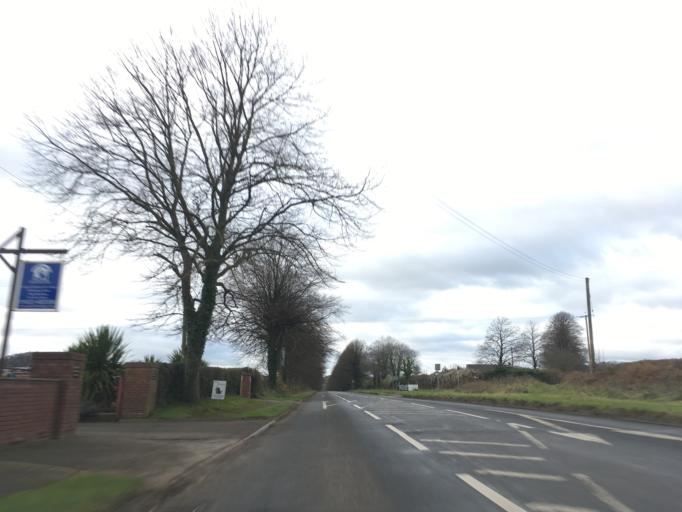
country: GB
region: Wales
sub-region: Newport
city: Llanvaches
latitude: 51.6160
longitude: -2.8168
